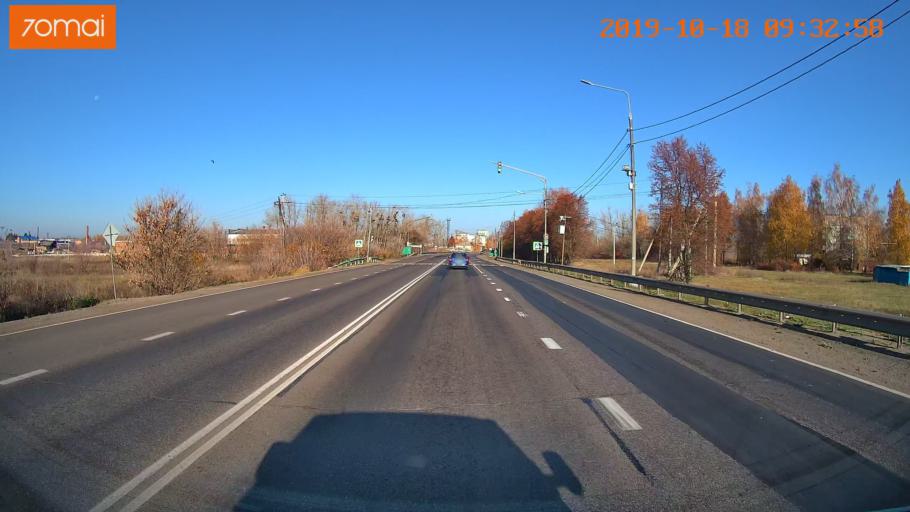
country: RU
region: Tula
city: Yefremov
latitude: 53.1624
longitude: 38.1540
